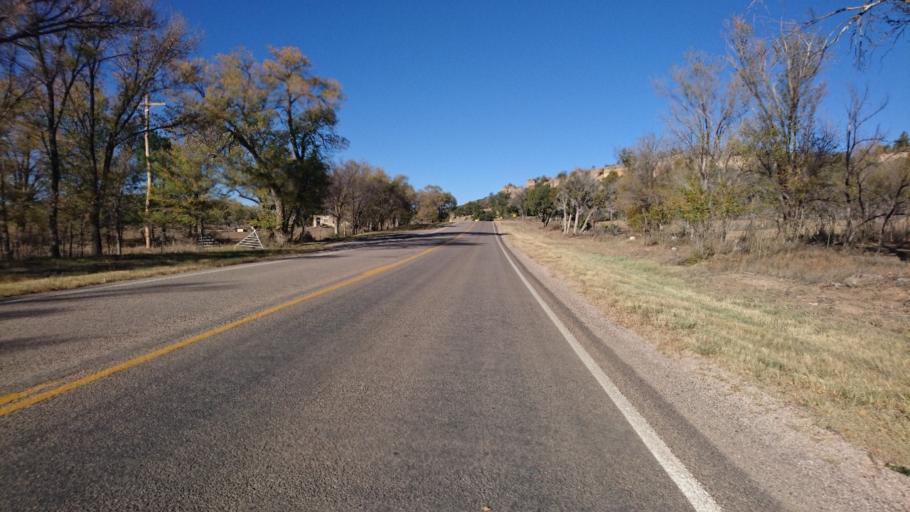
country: US
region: New Mexico
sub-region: McKinley County
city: Black Rock
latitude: 35.1333
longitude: -108.5131
